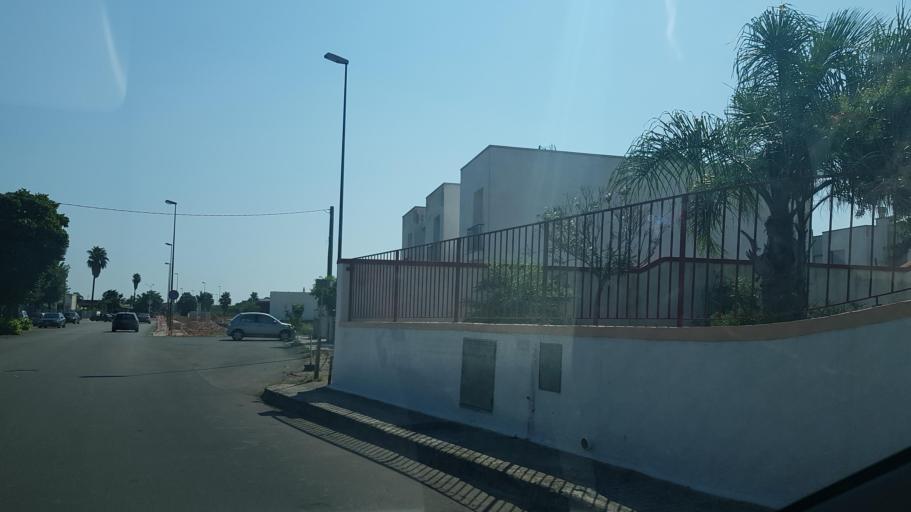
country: IT
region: Apulia
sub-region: Provincia di Lecce
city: Ruffano
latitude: 39.9857
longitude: 18.2557
